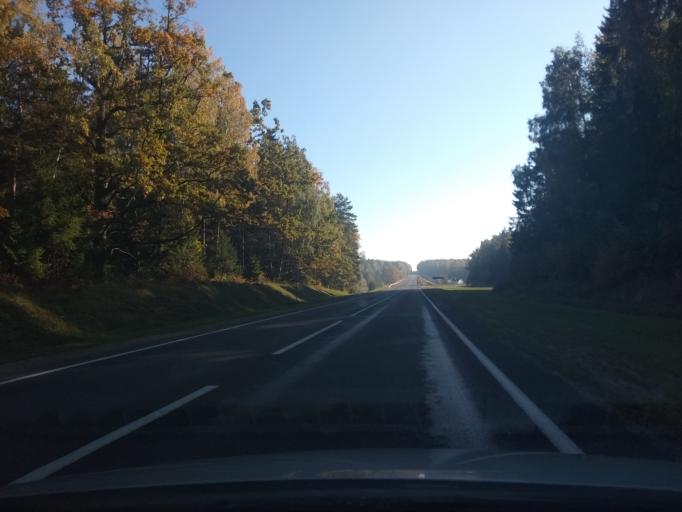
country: BY
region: Grodnenskaya
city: Zel'va
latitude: 53.1397
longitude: 24.9161
